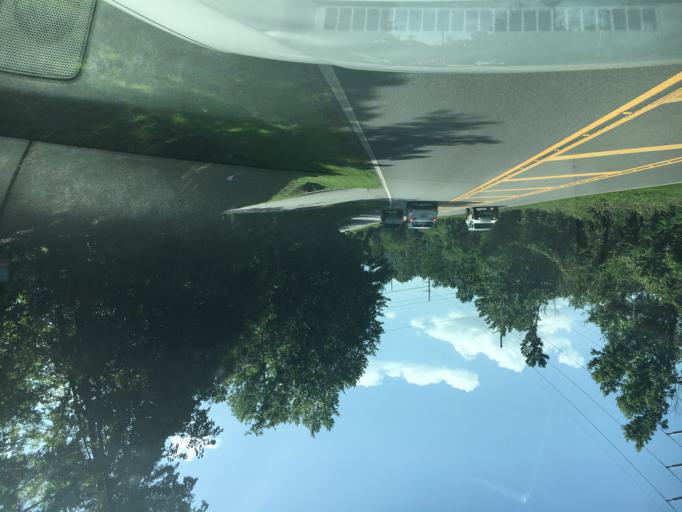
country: US
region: Alabama
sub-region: Shelby County
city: Meadowbrook
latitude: 33.4068
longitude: -86.7051
